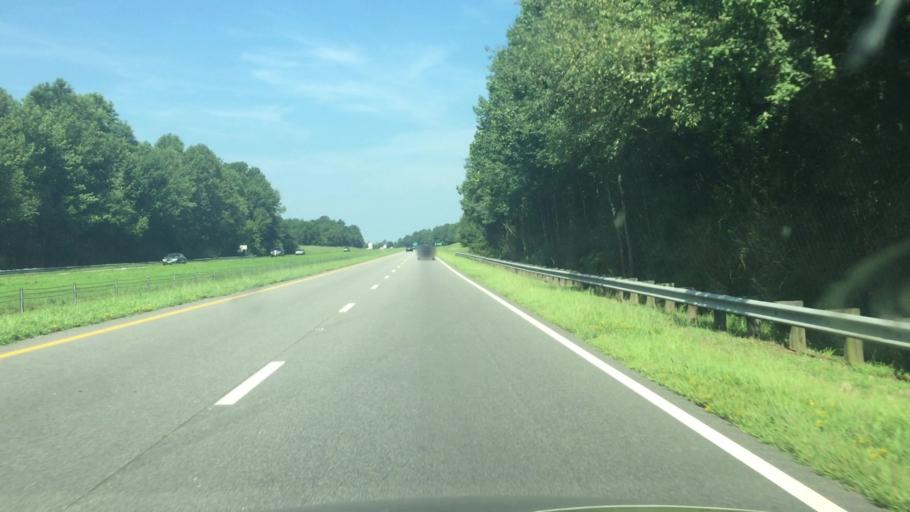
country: US
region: North Carolina
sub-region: Robeson County
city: Maxton
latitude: 34.7619
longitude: -79.3873
